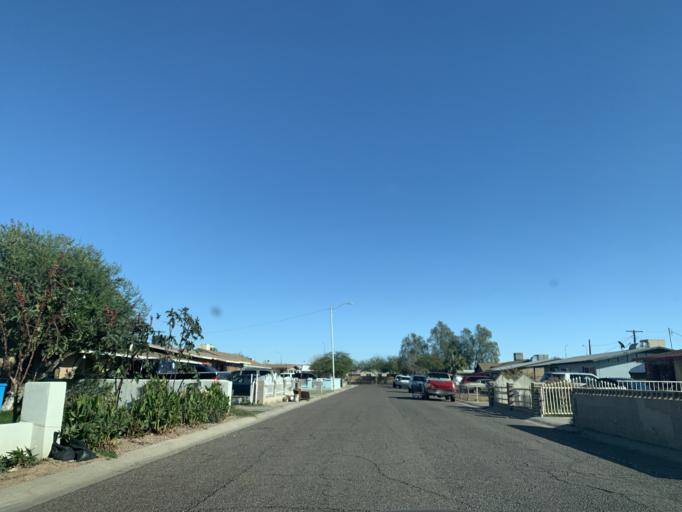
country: US
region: Arizona
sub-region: Maricopa County
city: Laveen
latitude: 33.3979
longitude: -112.1351
